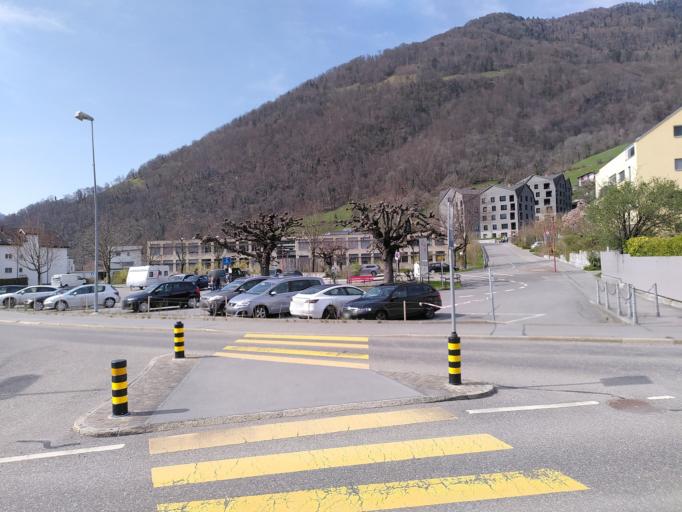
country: CH
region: Saint Gallen
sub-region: Wahlkreis See-Gaster
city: Weesen
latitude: 47.1330
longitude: 9.0932
